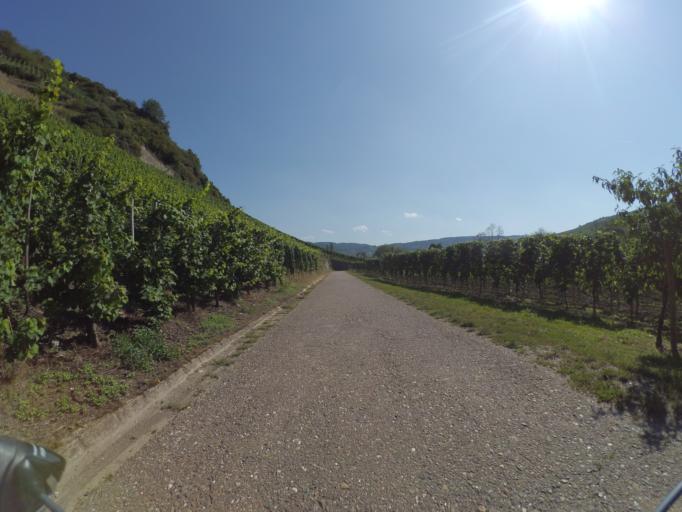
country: DE
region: Rheinland-Pfalz
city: Trittenheim
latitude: 49.8375
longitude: 6.8990
